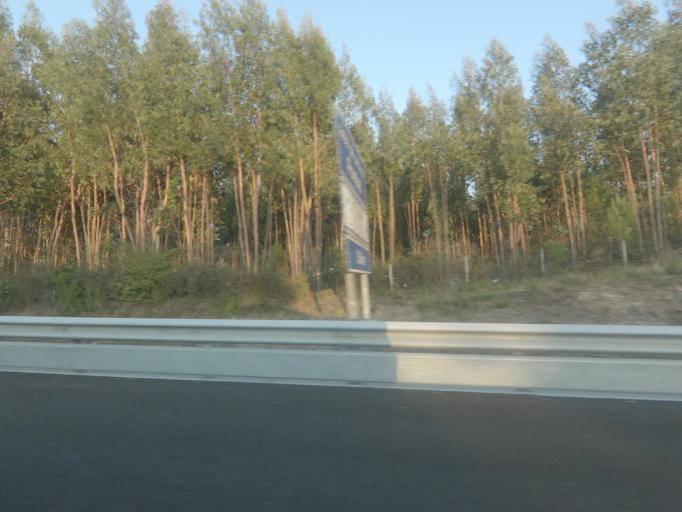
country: PT
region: Leiria
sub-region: Leiria
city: Caranguejeira
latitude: 39.7800
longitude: -8.7386
